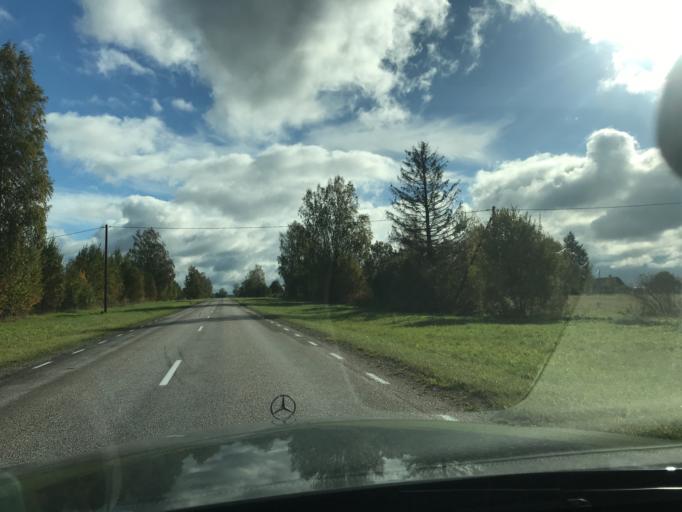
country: EE
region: Valgamaa
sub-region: Torva linn
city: Torva
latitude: 58.0113
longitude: 26.1823
